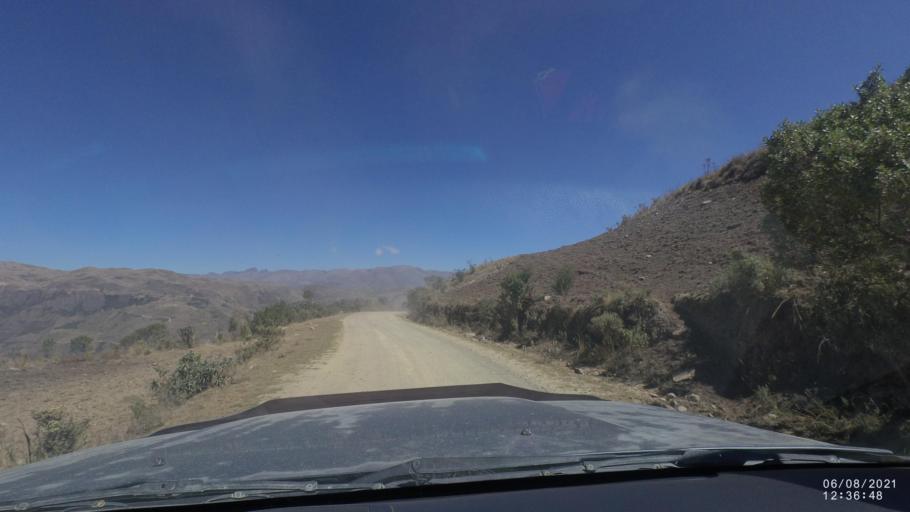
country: BO
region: Cochabamba
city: Colchani
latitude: -16.7795
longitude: -66.6559
